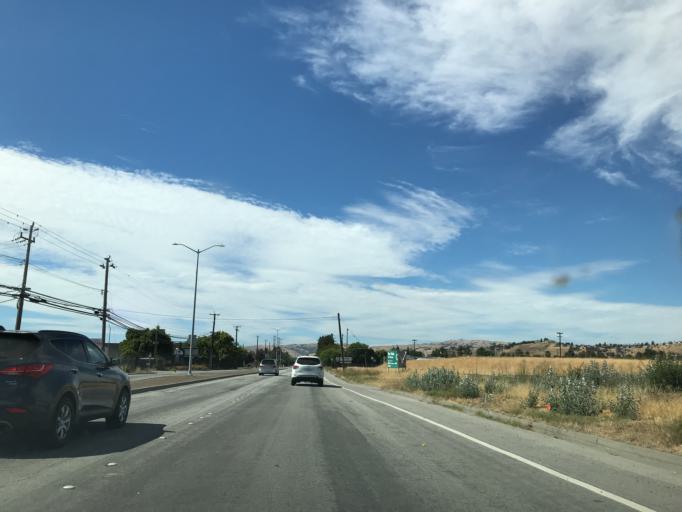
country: US
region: California
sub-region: Alameda County
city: Fremont
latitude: 37.5031
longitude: -121.9489
